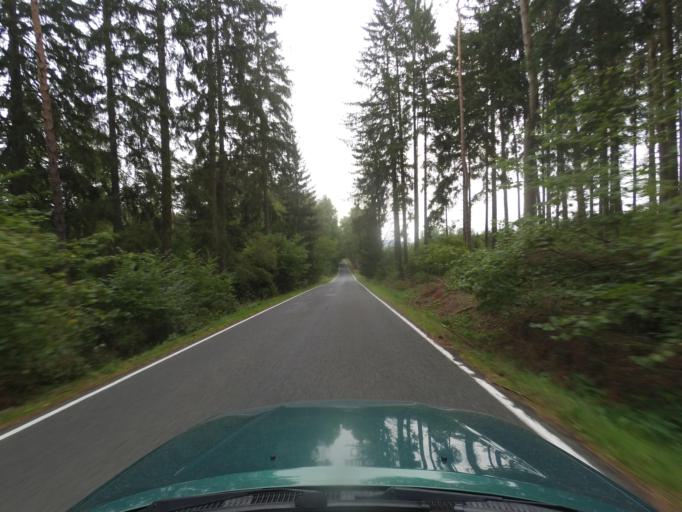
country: CZ
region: Plzensky
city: Bela nad Radbuzou
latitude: 49.5900
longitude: 12.6797
